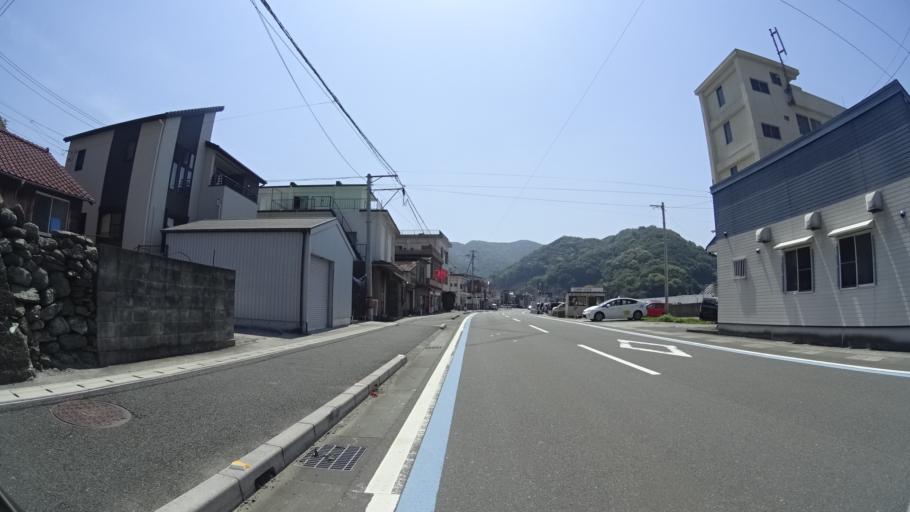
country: JP
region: Ehime
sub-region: Nishiuwa-gun
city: Ikata-cho
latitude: 33.3910
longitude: 132.1190
